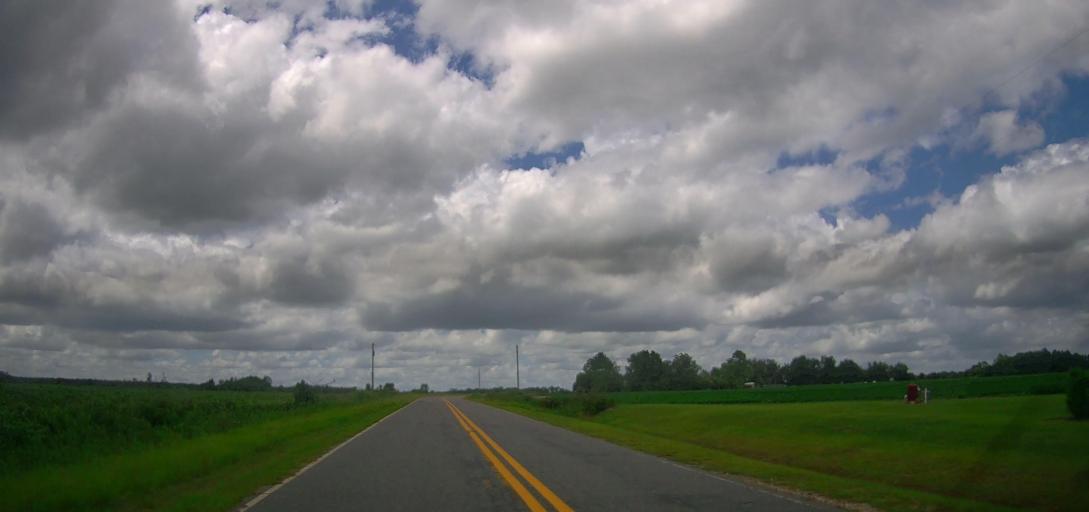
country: US
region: Georgia
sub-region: Irwin County
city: Ocilla
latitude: 31.6487
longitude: -83.3993
